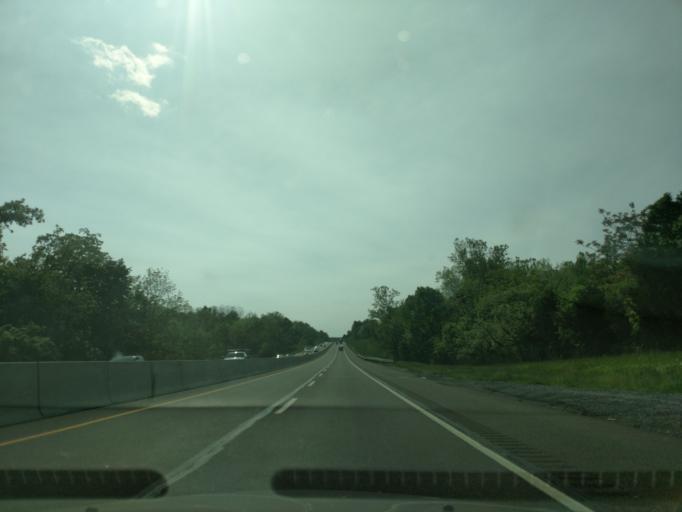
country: US
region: Pennsylvania
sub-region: Lancaster County
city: Schoeneck
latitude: 40.2442
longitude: -76.1607
